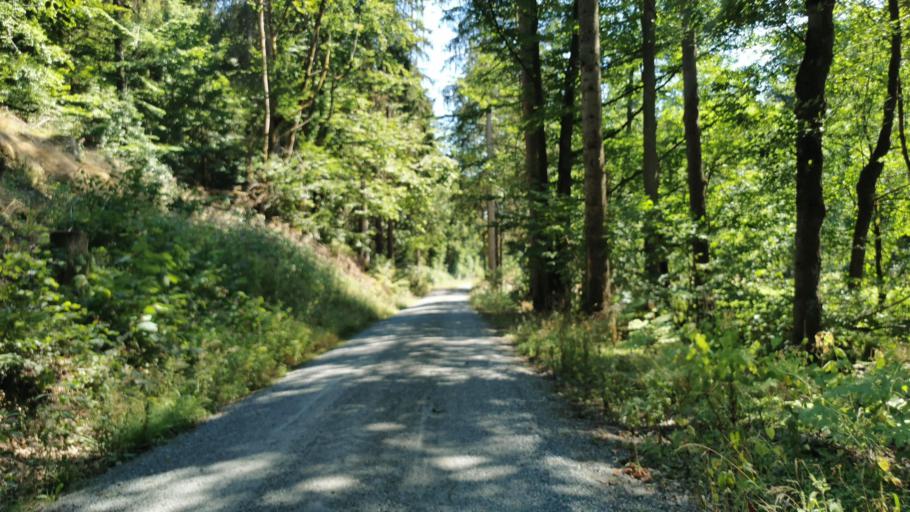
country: DE
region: Bavaria
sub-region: Upper Franconia
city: Pressig
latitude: 50.3851
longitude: 11.2964
